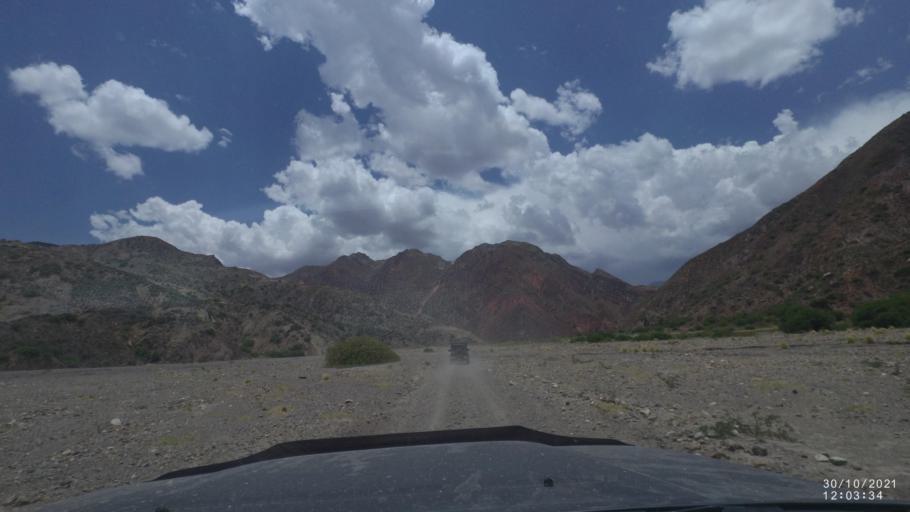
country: BO
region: Cochabamba
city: Colchani
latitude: -17.5270
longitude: -66.6204
